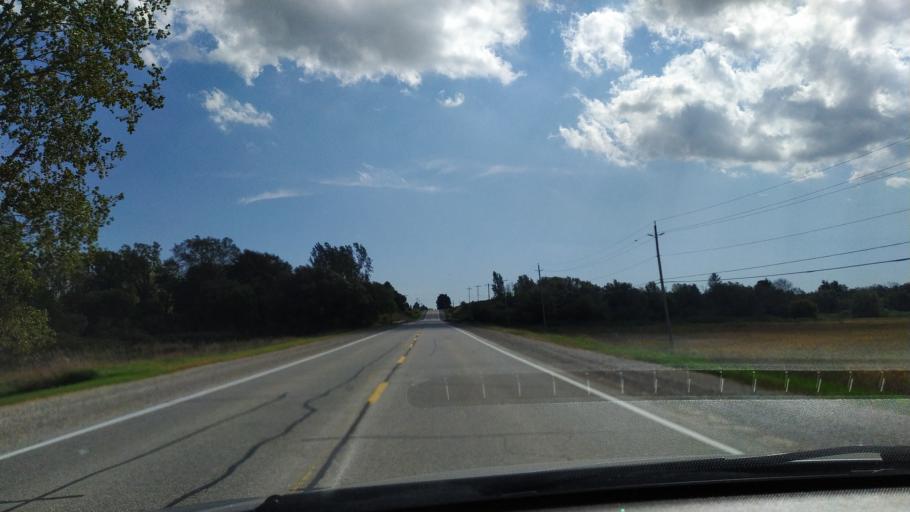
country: CA
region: Ontario
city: Ingersoll
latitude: 43.1404
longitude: -80.8936
